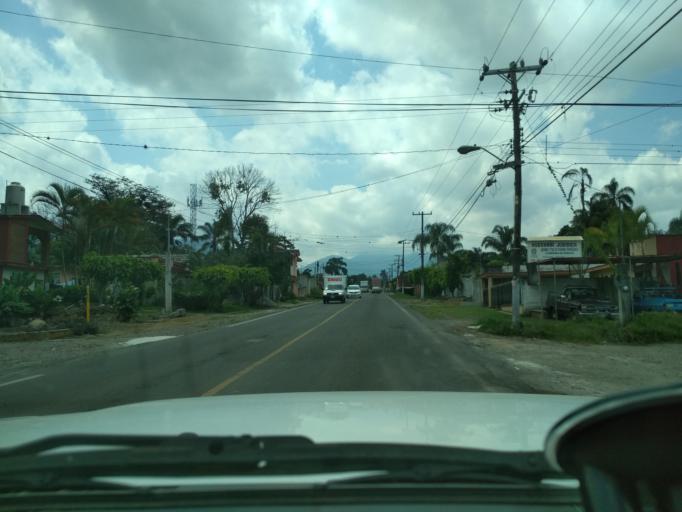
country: MX
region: Veracruz
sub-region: Fortin
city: Monte Salas
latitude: 18.9356
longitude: -97.0172
